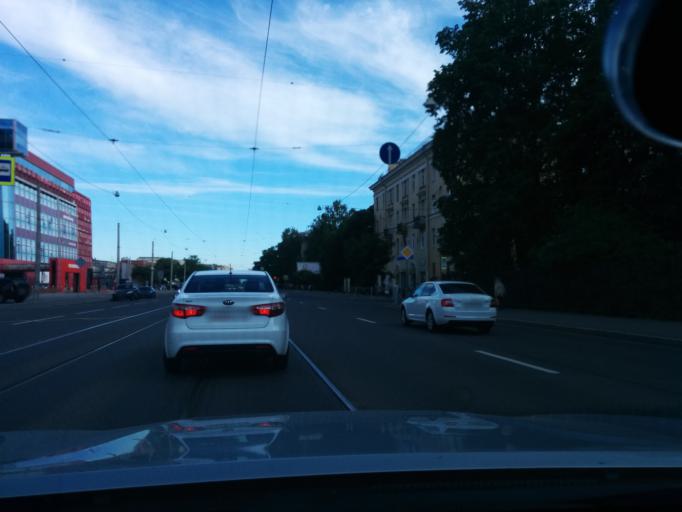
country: RU
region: Leningrad
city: Udel'naya
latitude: 60.0107
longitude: 30.3248
